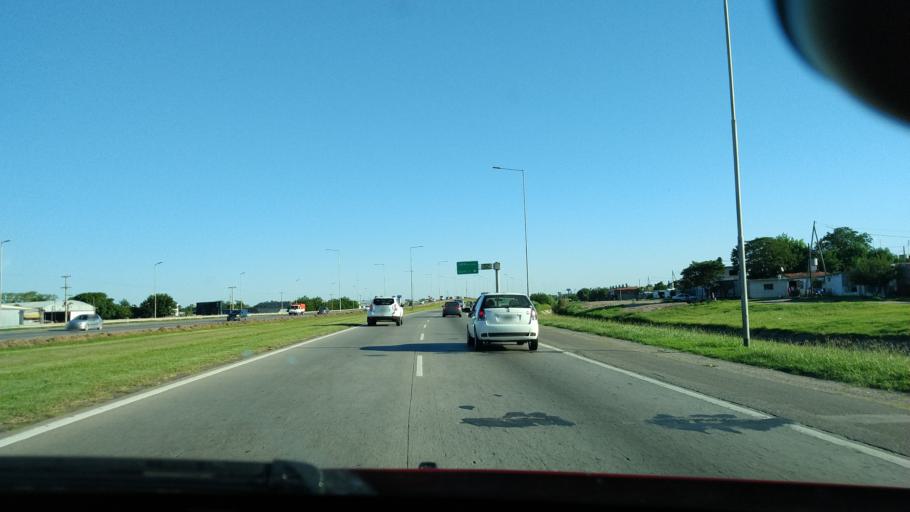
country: AR
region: Cordoba
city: Malvinas Argentinas
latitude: -31.3716
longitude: -64.1281
